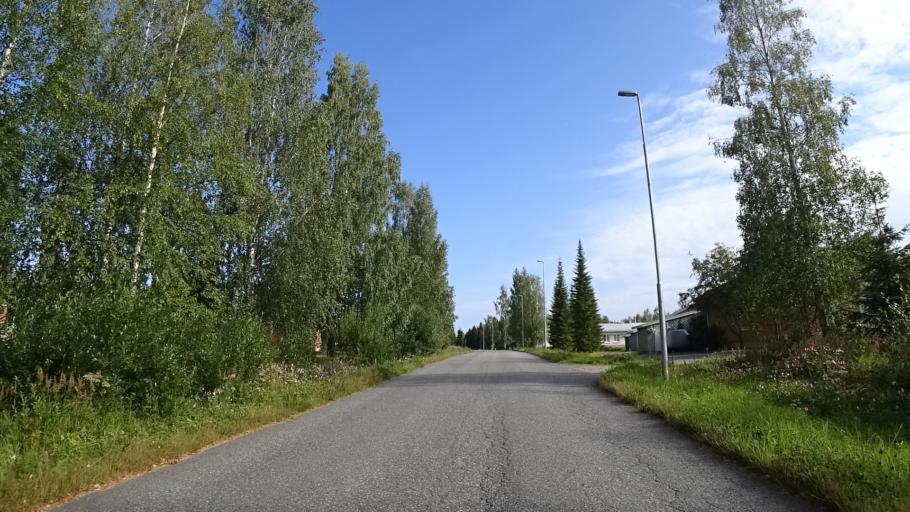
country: FI
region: North Karelia
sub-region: Joensuu
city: Eno
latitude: 62.7959
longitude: 30.1392
